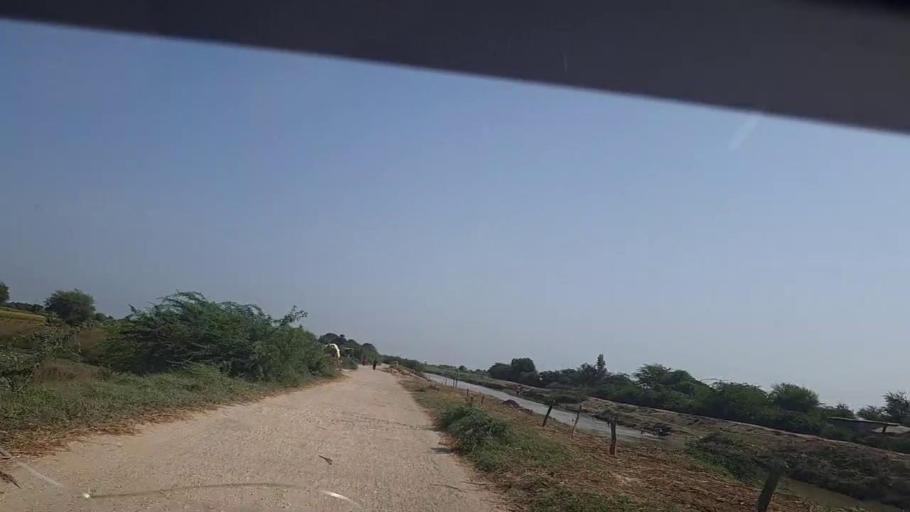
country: PK
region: Sindh
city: Rajo Khanani
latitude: 24.9750
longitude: 68.8686
